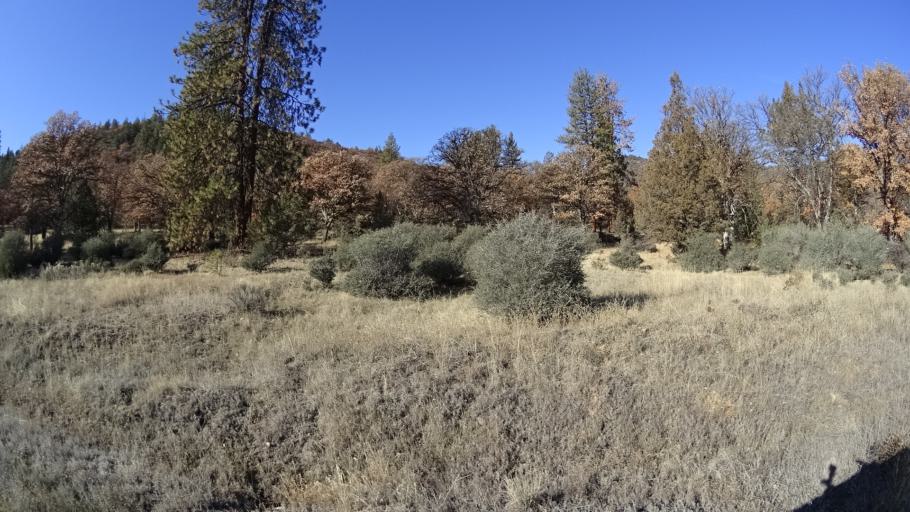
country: US
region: California
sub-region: Siskiyou County
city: Yreka
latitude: 41.6980
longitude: -122.6510
